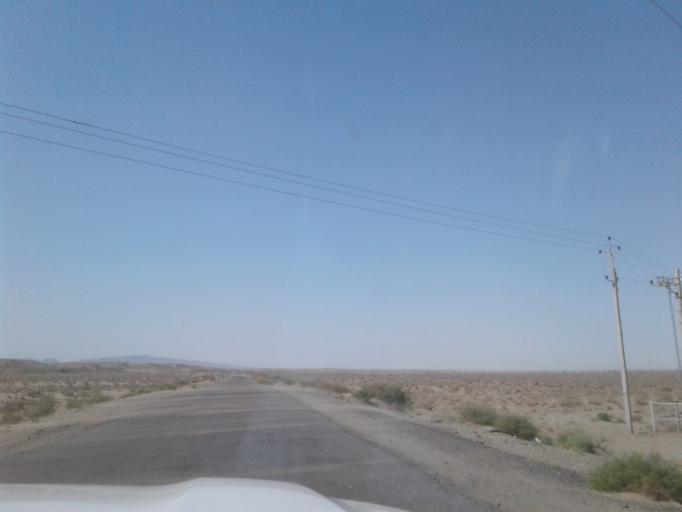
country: TM
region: Balkan
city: Gazanjyk
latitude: 39.2535
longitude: 55.3077
